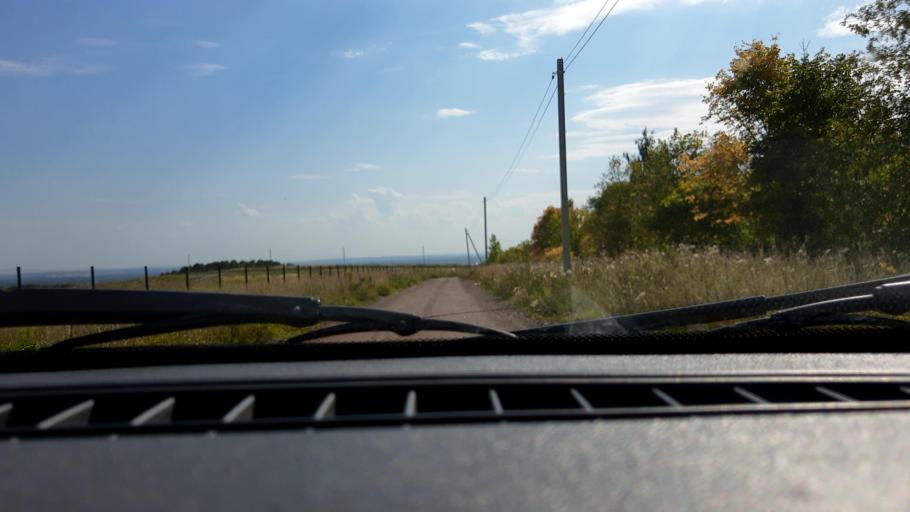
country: RU
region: Bashkortostan
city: Ufa
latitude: 54.8523
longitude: 56.1633
